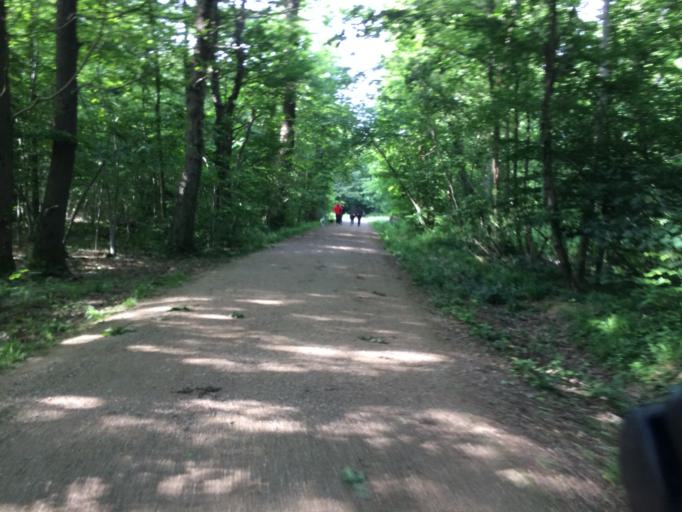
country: FR
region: Ile-de-France
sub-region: Departement de l'Essonne
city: Igny
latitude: 48.7547
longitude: 2.2421
